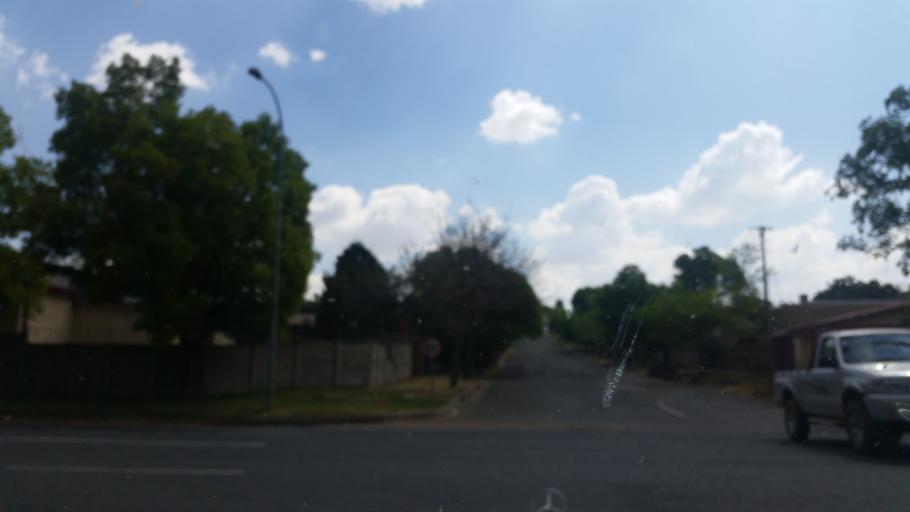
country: ZA
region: Orange Free State
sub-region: Thabo Mofutsanyana District Municipality
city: Reitz
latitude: -27.8032
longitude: 28.4276
